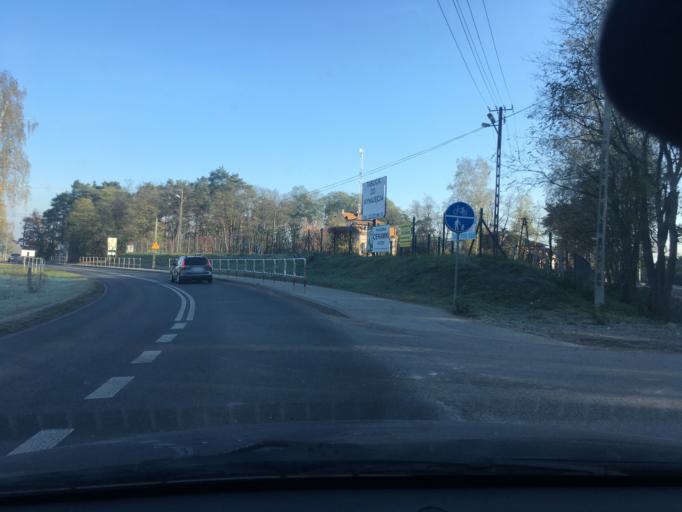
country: PL
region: Masovian Voivodeship
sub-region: Powiat piaseczynski
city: Lesznowola
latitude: 52.0668
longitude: 20.9335
